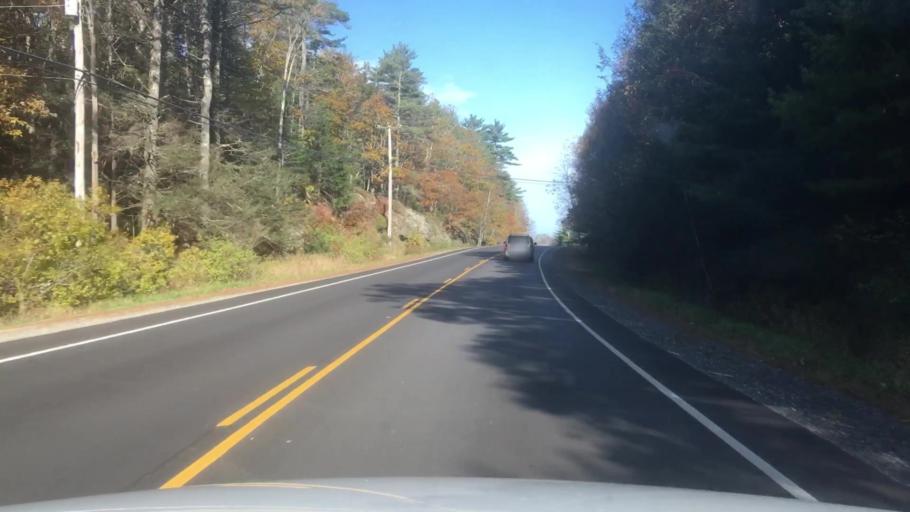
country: US
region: Maine
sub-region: Sagadahoc County
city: Woolwich
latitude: 43.8958
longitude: -69.7946
